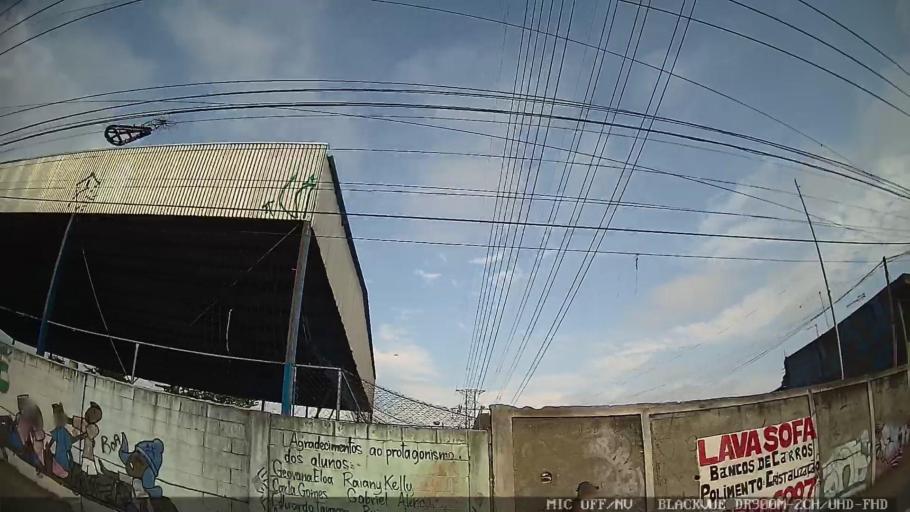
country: BR
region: Sao Paulo
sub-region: Ferraz De Vasconcelos
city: Ferraz de Vasconcelos
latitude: -23.5143
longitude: -46.4026
